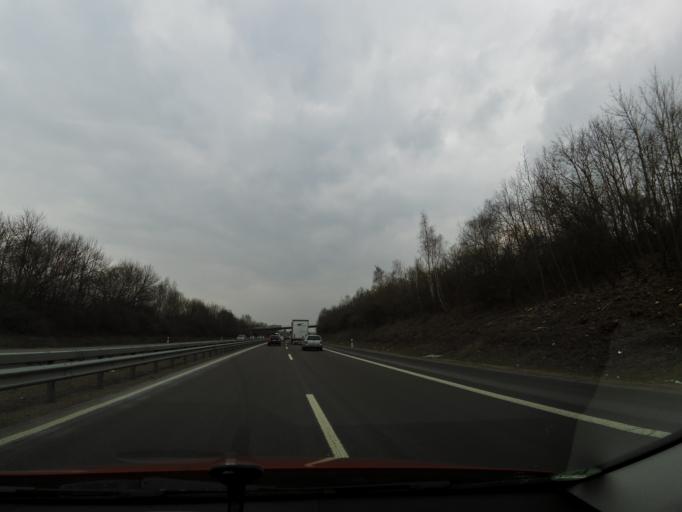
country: DE
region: Rheinland-Pfalz
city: Alzey
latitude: 49.7415
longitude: 8.1378
